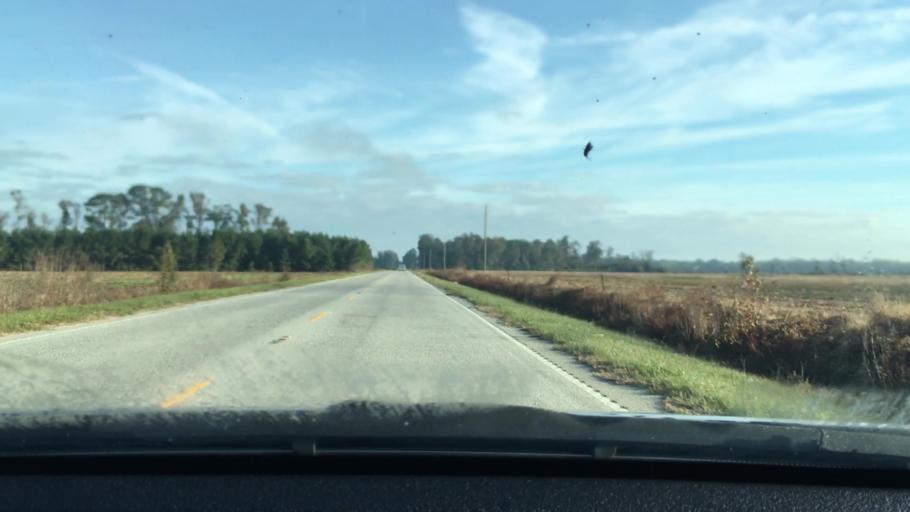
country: US
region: South Carolina
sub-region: Sumter County
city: East Sumter
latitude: 34.0133
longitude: -80.2836
